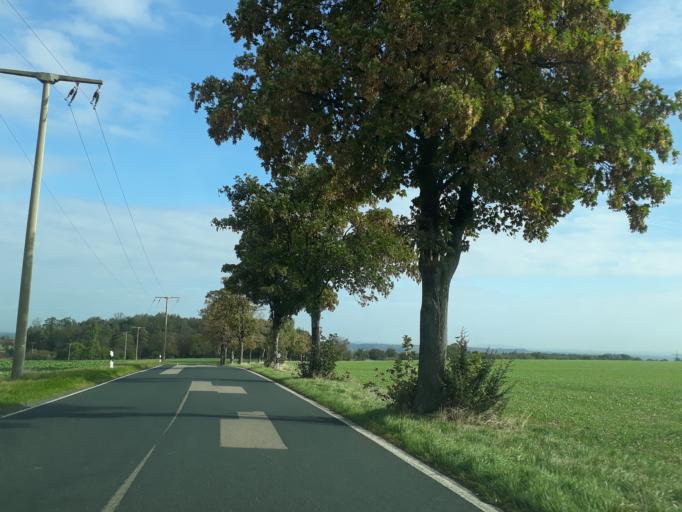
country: DE
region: Saxony
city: Wilsdruff
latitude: 51.0712
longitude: 13.5752
